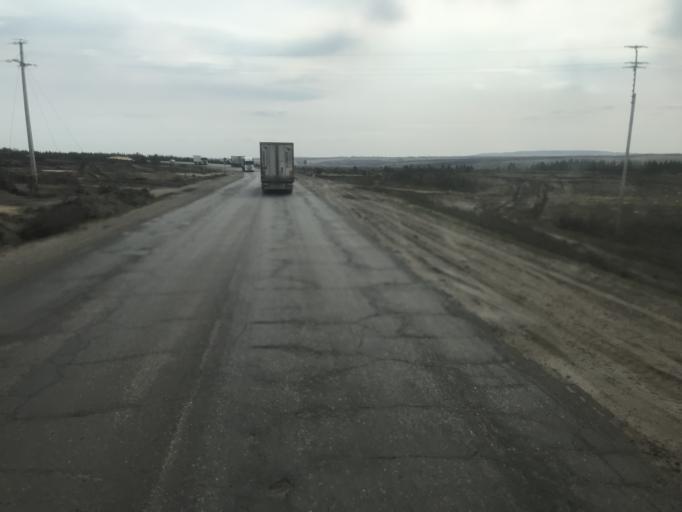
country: RU
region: Ulyanovsk
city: Novospasskoye
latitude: 53.1507
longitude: 47.6490
